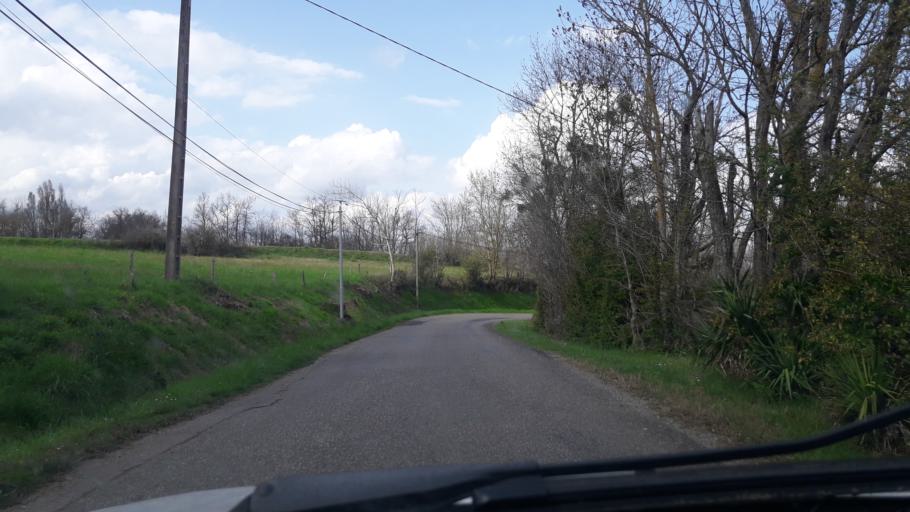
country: FR
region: Midi-Pyrenees
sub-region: Departement de l'Ariege
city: Lezat-sur-Leze
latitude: 43.1794
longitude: 1.3321
